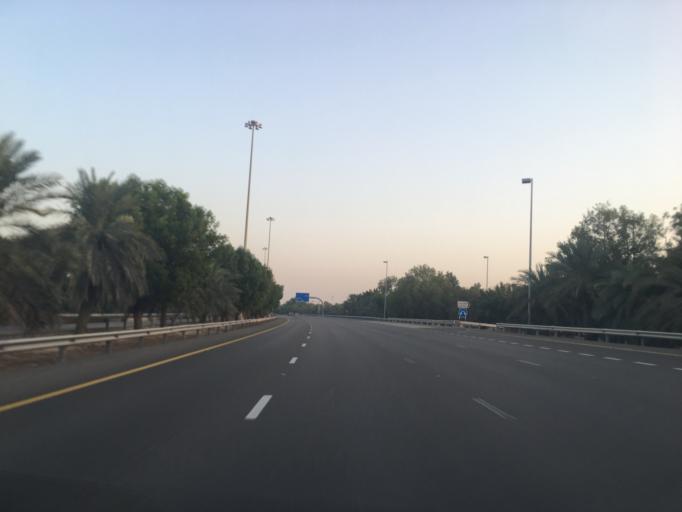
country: AE
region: Abu Dhabi
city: Abu Dhabi
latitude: 24.3606
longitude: 54.5649
